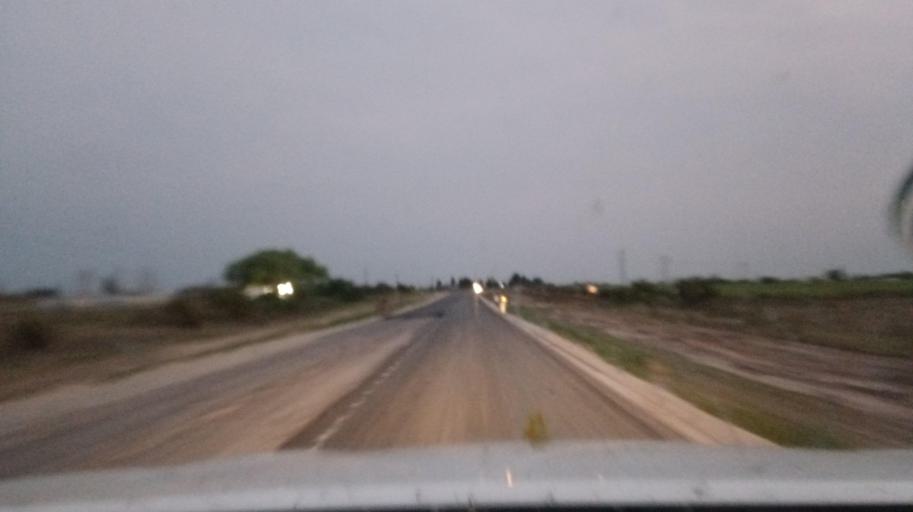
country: UY
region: Canelones
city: Sauce
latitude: -34.5711
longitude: -56.1011
